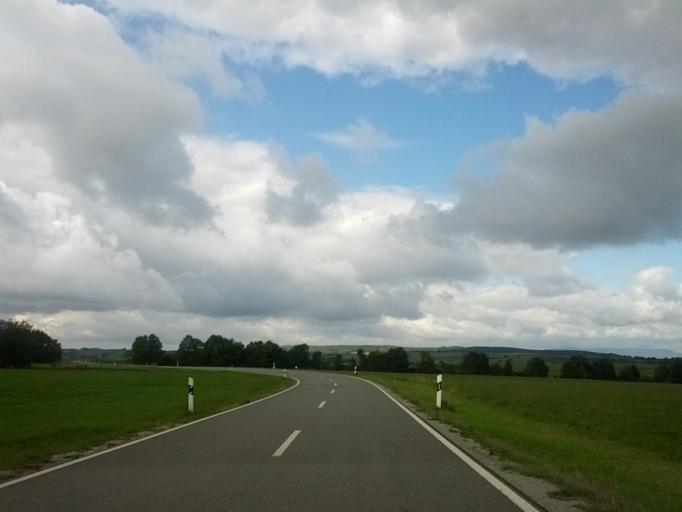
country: DE
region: Hesse
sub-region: Regierungsbezirk Kassel
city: Weissenborn
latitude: 51.0643
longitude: 10.1000
